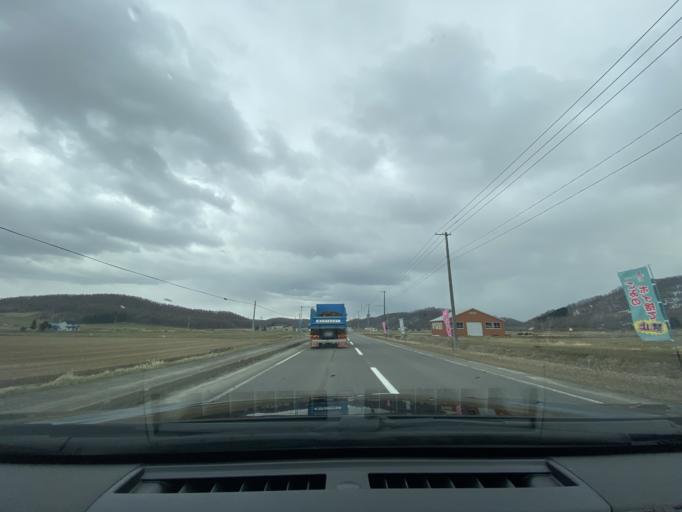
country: JP
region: Hokkaido
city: Nayoro
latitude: 44.1797
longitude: 142.2865
